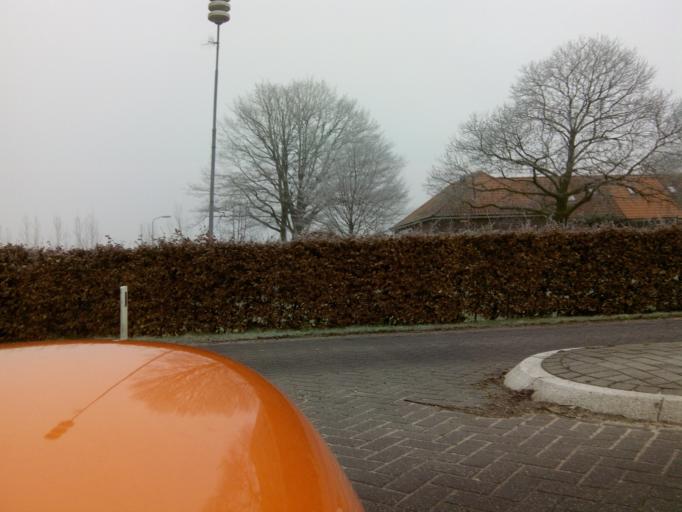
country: NL
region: Gelderland
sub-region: Gemeente Barneveld
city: Garderen
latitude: 52.2670
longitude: 5.7041
